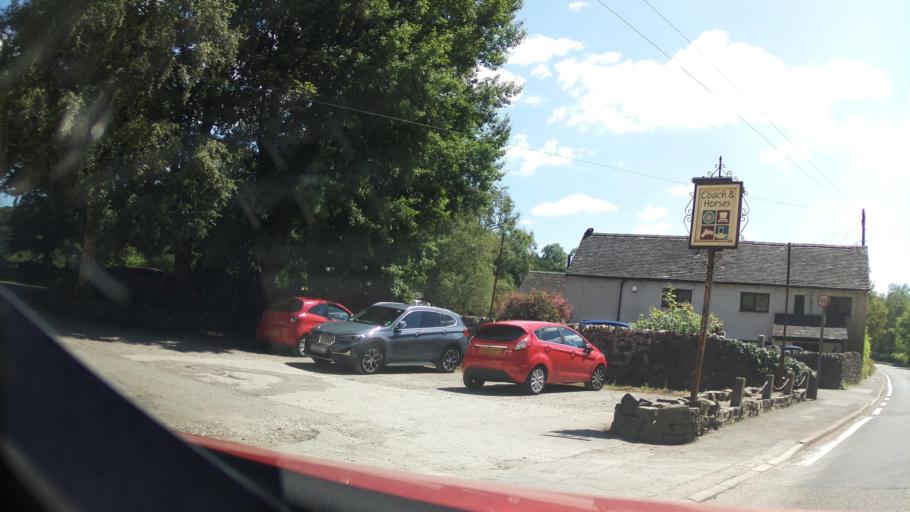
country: GB
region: England
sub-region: Derbyshire
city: Ashbourne
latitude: 53.0474
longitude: -1.7396
